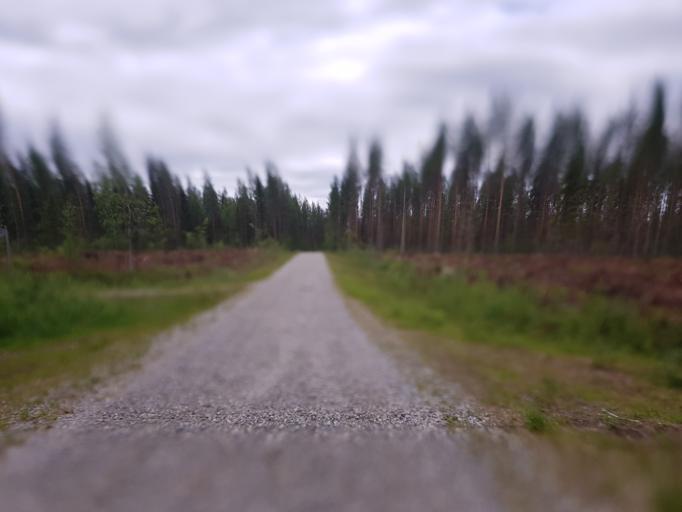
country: FI
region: Kainuu
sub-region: Kehys-Kainuu
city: Kuhmo
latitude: 64.4517
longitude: 29.7243
